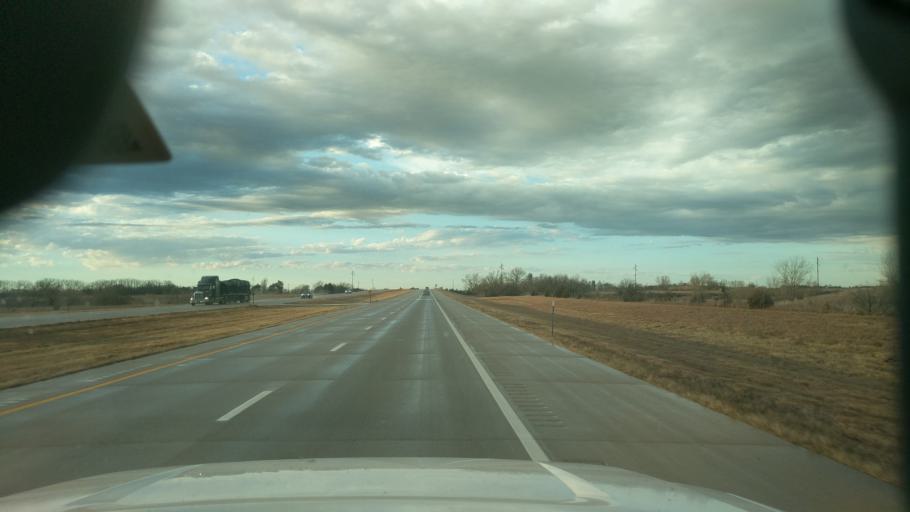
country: US
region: Kansas
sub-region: Harvey County
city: Hesston
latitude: 38.1120
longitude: -97.3837
